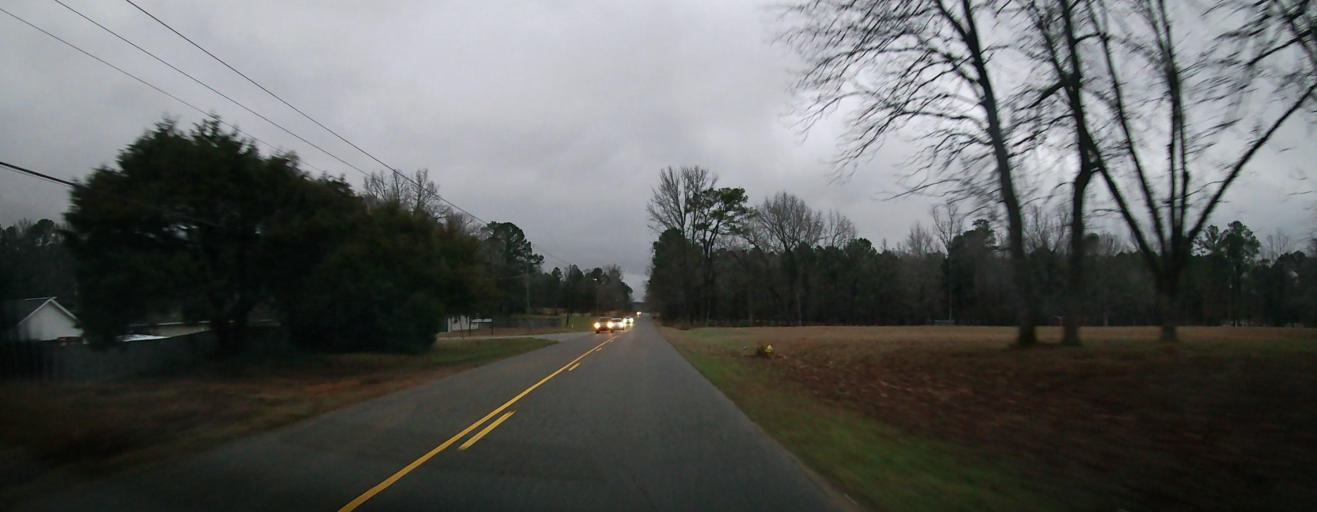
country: US
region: Alabama
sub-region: Tuscaloosa County
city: Vance
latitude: 33.1446
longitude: -87.2298
